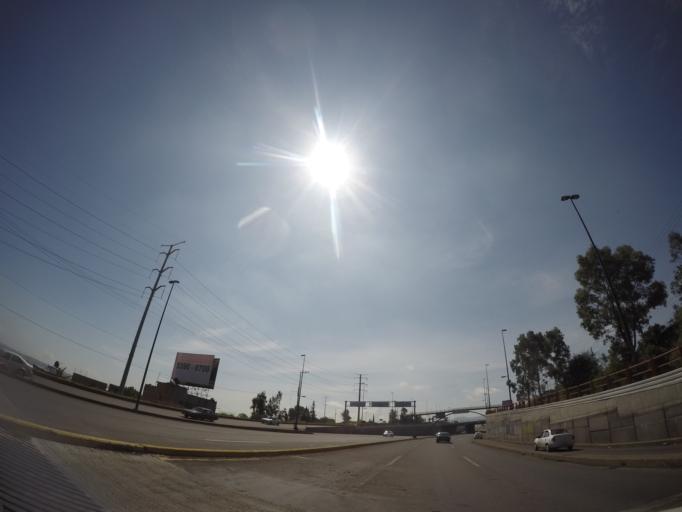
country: MX
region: Michoacan
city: Morelia
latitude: 19.7242
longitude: -101.1952
